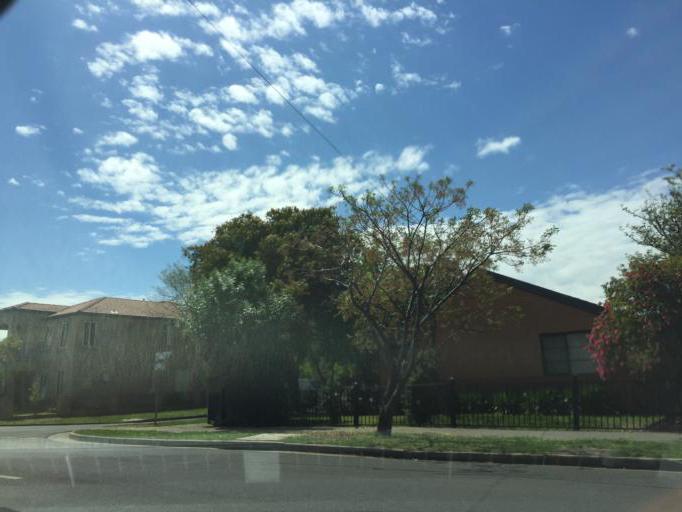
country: AU
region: Victoria
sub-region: Maribyrnong
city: Braybrook
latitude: -37.7806
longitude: 144.8469
